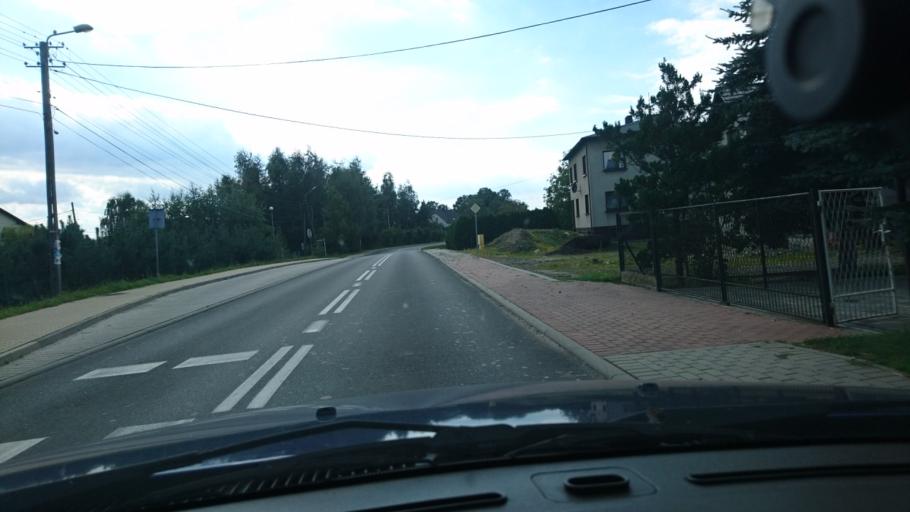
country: PL
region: Silesian Voivodeship
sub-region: Powiat bielski
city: Ligota
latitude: 49.8993
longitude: 18.9664
